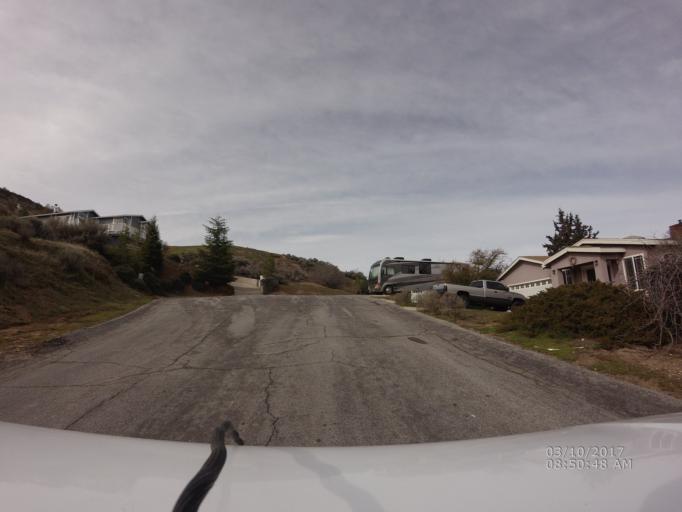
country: US
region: California
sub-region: Los Angeles County
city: Green Valley
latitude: 34.6608
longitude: -118.3903
